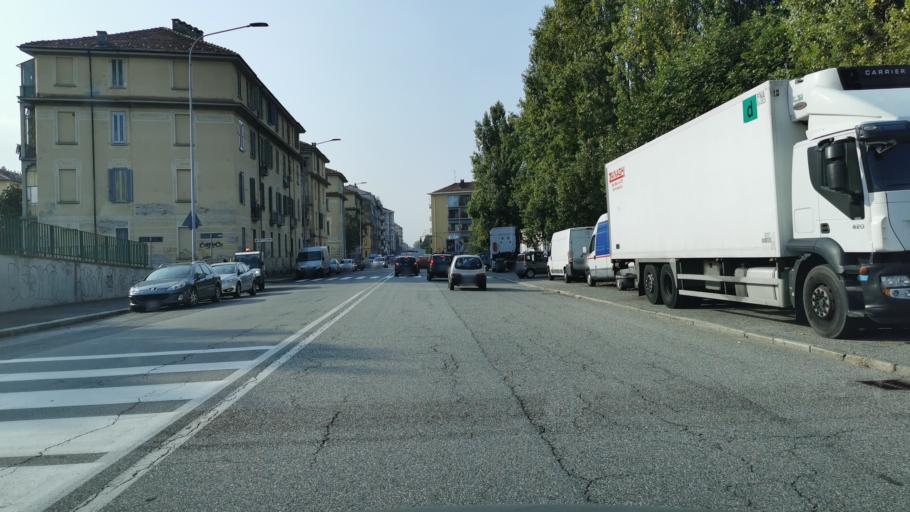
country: IT
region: Piedmont
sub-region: Provincia di Torino
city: Turin
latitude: 45.0979
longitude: 7.6896
